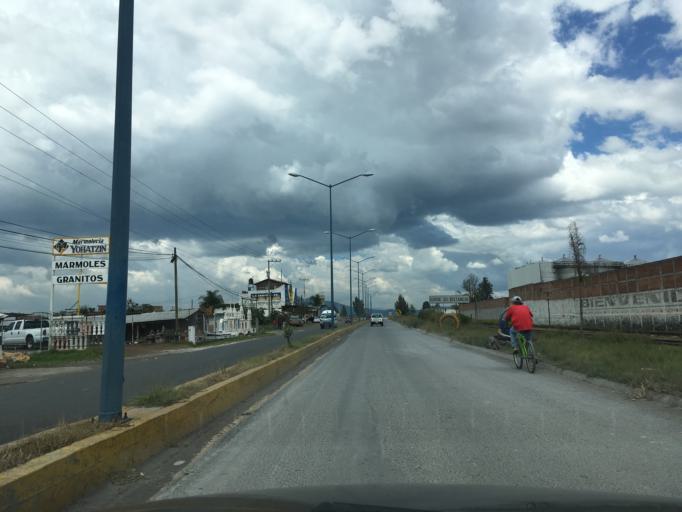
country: MX
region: Michoacan
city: Zacapu
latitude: 19.8368
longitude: -101.7693
